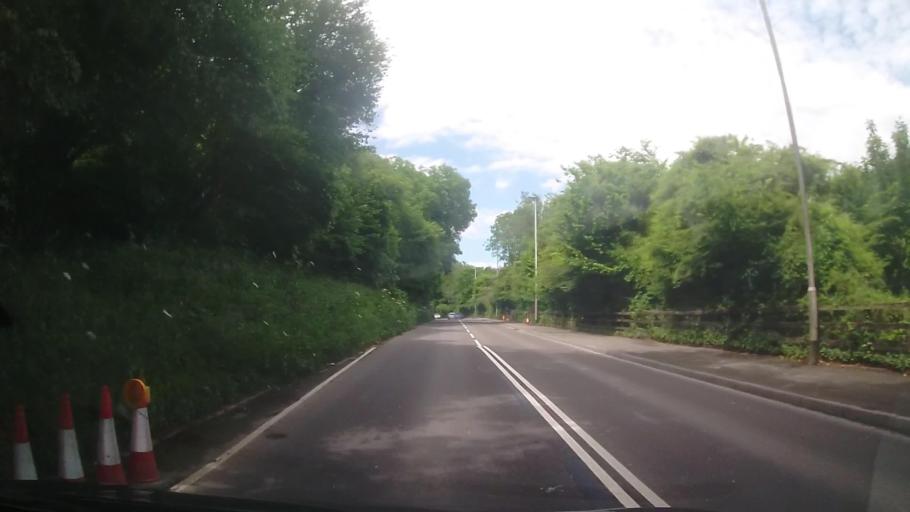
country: GB
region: England
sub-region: Devon
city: Plympton
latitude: 50.3998
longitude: -4.0987
